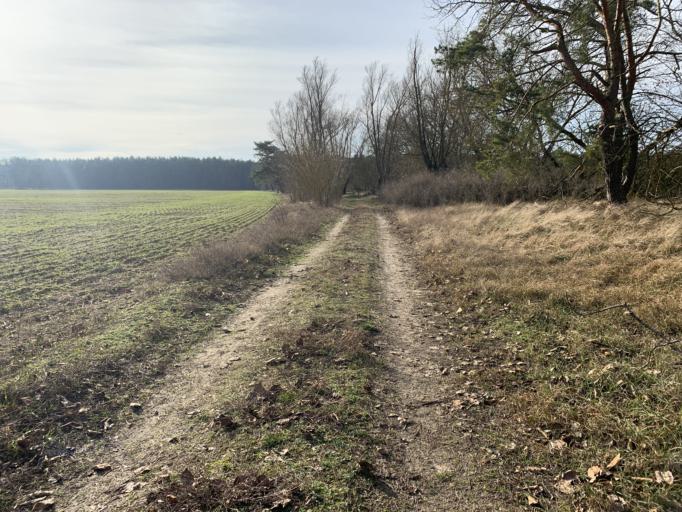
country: DE
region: Mecklenburg-Vorpommern
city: Wesenberg
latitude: 53.2898
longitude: 12.8674
